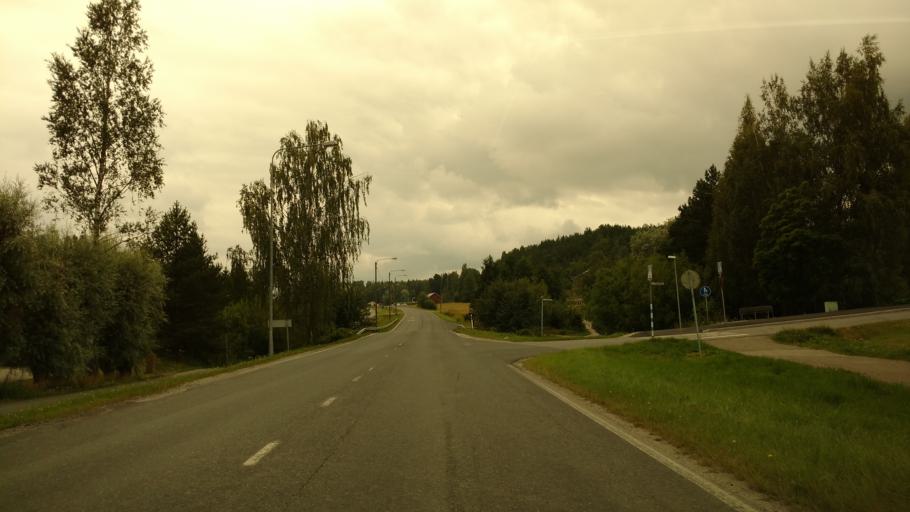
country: FI
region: Varsinais-Suomi
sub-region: Salo
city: Halikko
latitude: 60.4037
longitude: 23.0700
